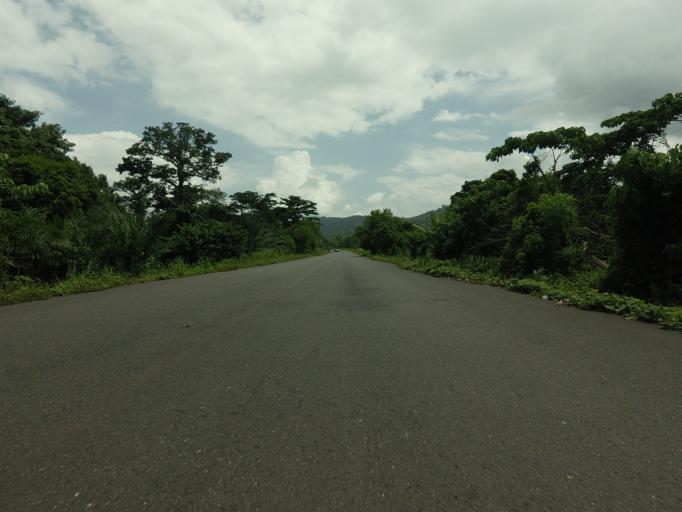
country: GH
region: Volta
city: Ho
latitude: 6.5401
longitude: 0.2387
